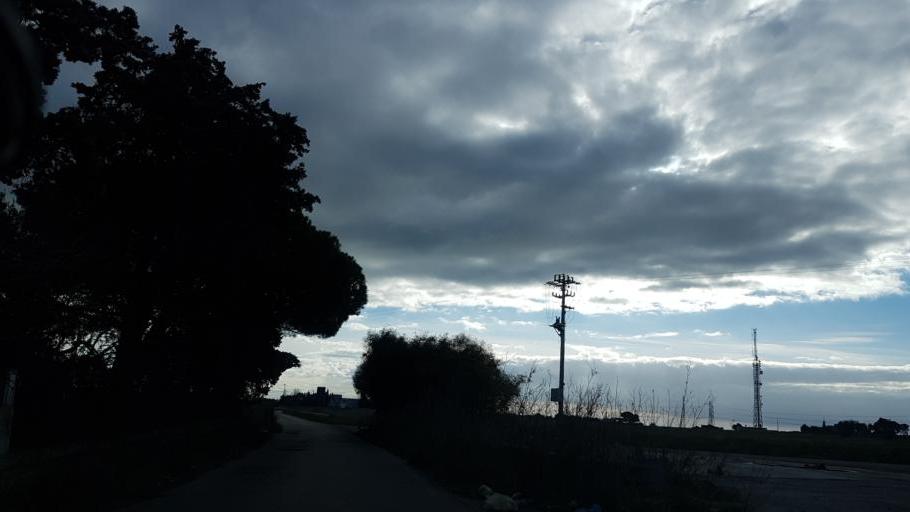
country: IT
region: Apulia
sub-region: Provincia di Brindisi
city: La Rosa
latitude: 40.6144
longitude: 17.9566
